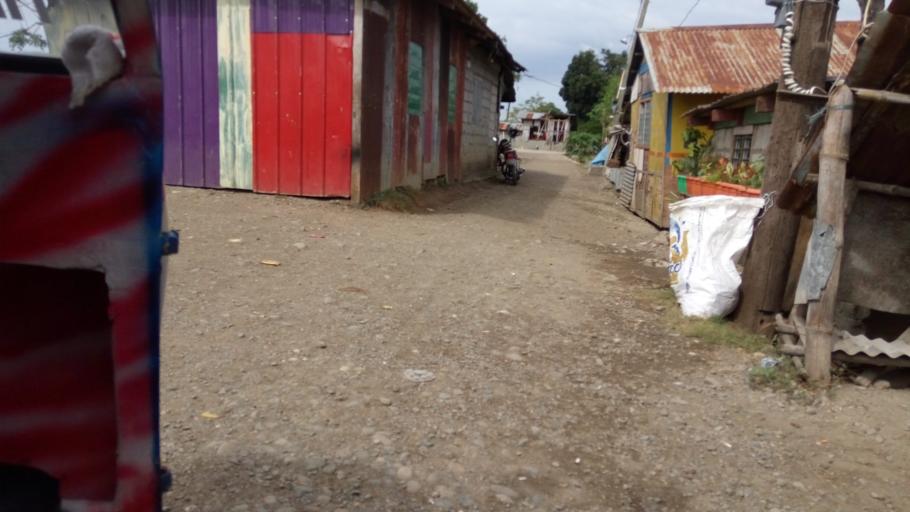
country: PH
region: Ilocos
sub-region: Province of La Union
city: Aringay
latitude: 16.3979
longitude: 120.3519
